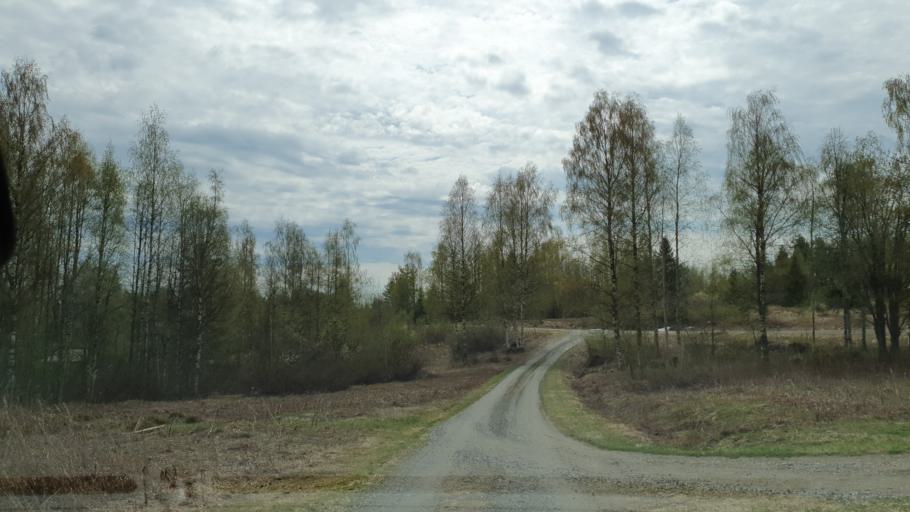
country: FI
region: Kainuu
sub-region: Kehys-Kainuu
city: Kuhmo
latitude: 64.1393
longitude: 29.9703
